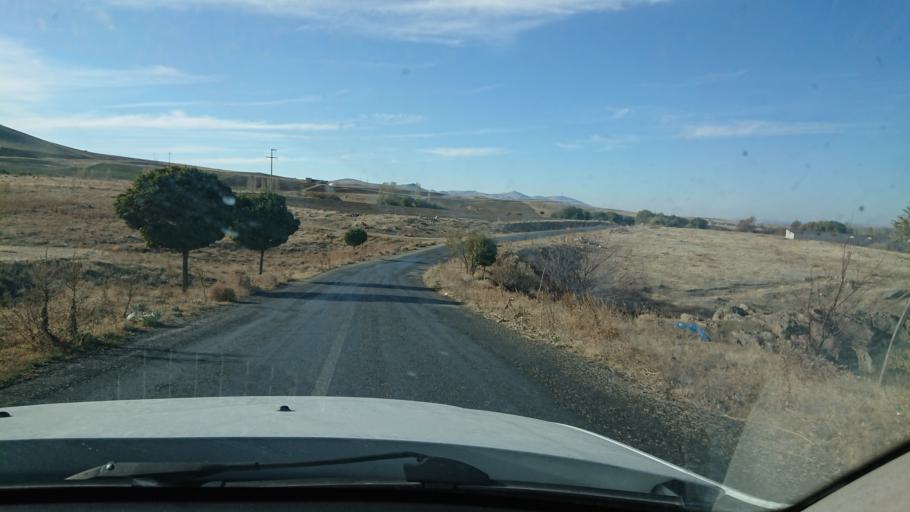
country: TR
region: Aksaray
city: Sariyahsi
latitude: 38.9682
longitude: 33.8701
